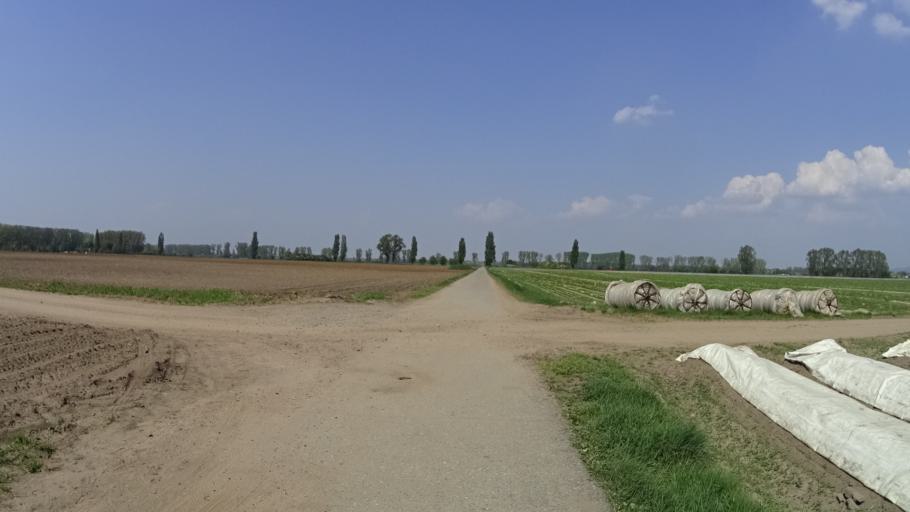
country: DE
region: Hesse
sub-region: Regierungsbezirk Darmstadt
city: Einhausen
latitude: 49.6630
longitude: 8.5149
